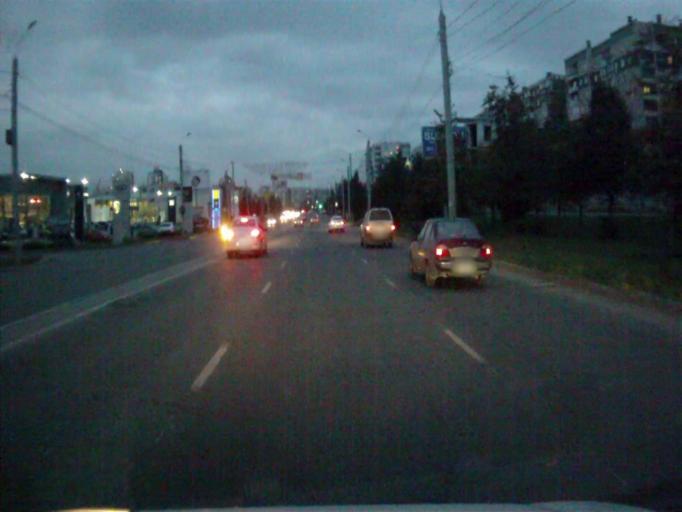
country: RU
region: Chelyabinsk
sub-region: Gorod Chelyabinsk
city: Chelyabinsk
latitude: 55.1723
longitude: 61.3018
